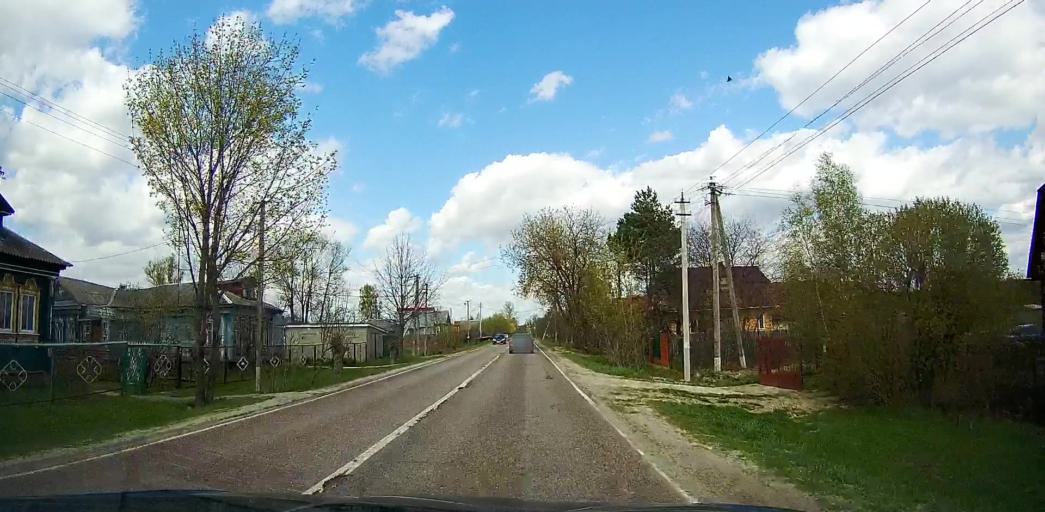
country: RU
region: Moskovskaya
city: Davydovo
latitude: 55.5814
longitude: 38.8252
